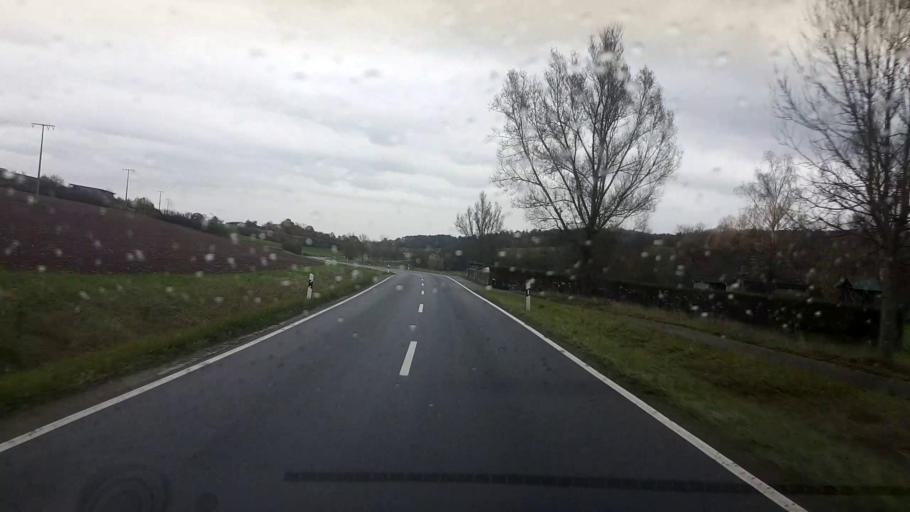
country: DE
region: Bavaria
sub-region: Upper Franconia
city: Burgwindheim
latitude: 49.8827
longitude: 10.5902
